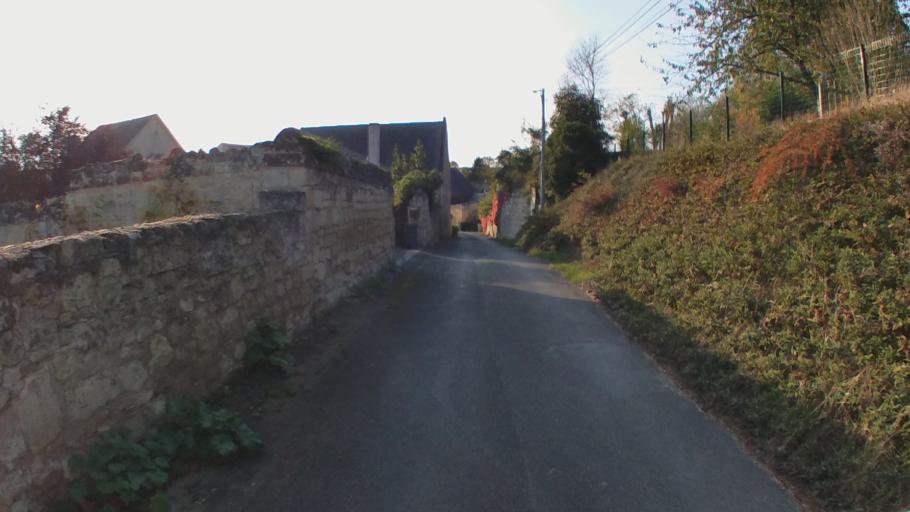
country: FR
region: Pays de la Loire
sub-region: Departement de Maine-et-Loire
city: Villebernier
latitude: 47.2320
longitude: 0.0027
